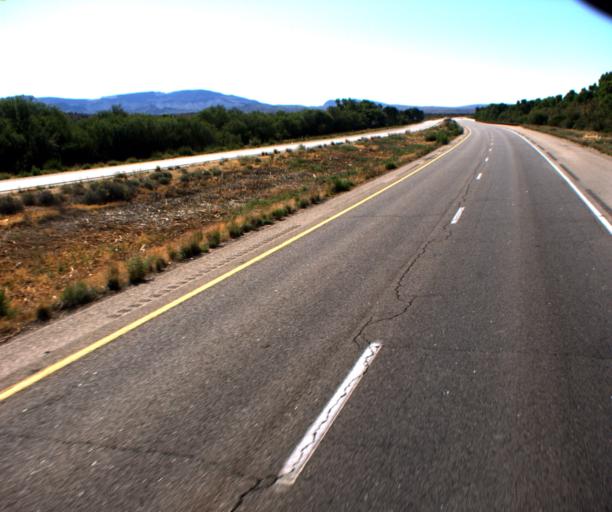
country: US
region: Arizona
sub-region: Yavapai County
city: Bagdad
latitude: 34.6672
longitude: -113.5858
